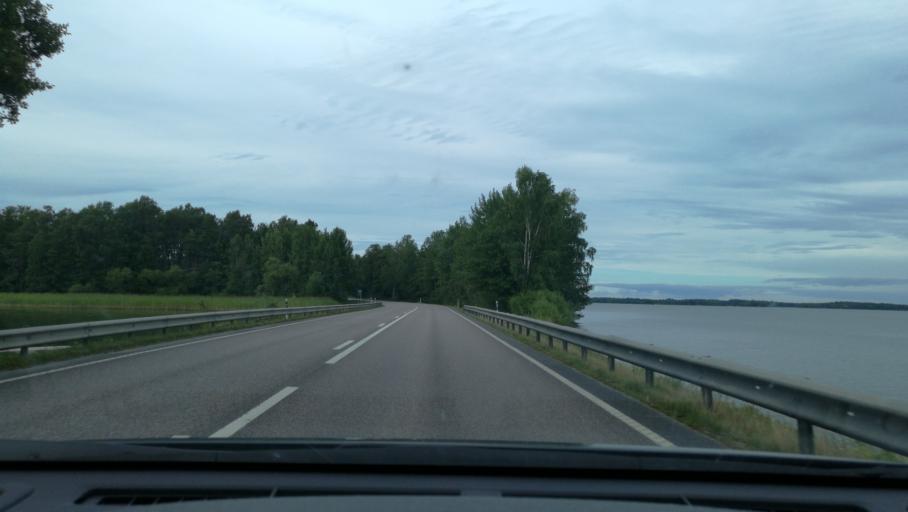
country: SE
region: Vaestmanland
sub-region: Kungsors Kommun
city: Kungsoer
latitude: 59.2492
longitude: 16.1070
